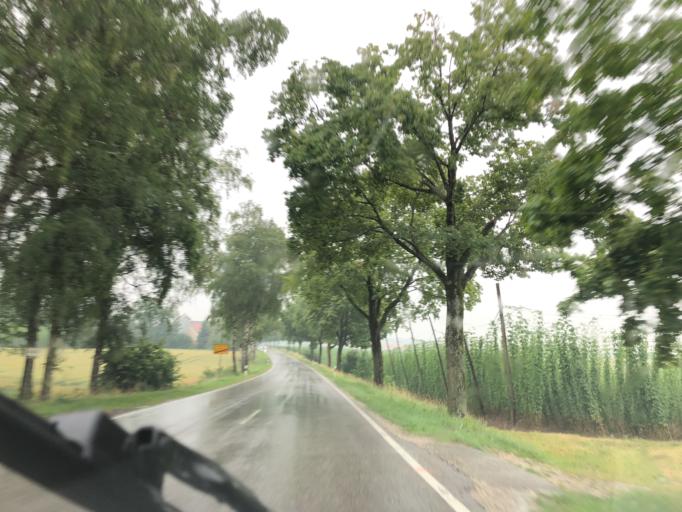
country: DE
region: Bavaria
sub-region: Upper Bavaria
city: Wolfersdorf
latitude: 48.5346
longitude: 11.7562
